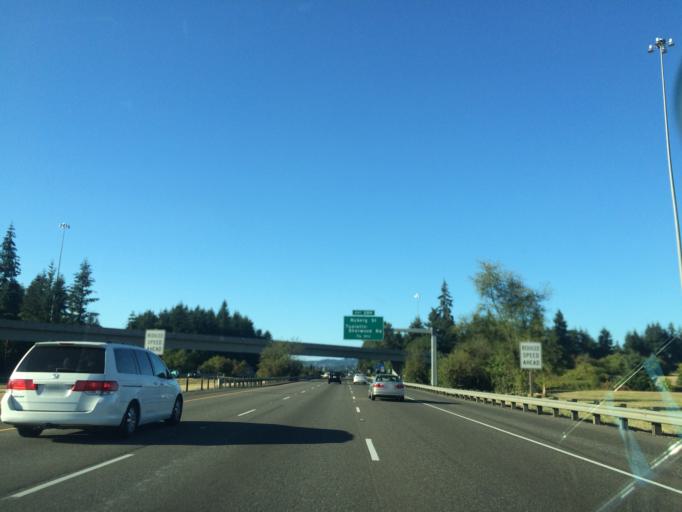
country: US
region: Oregon
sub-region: Washington County
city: Tualatin
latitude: 45.3673
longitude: -122.7584
